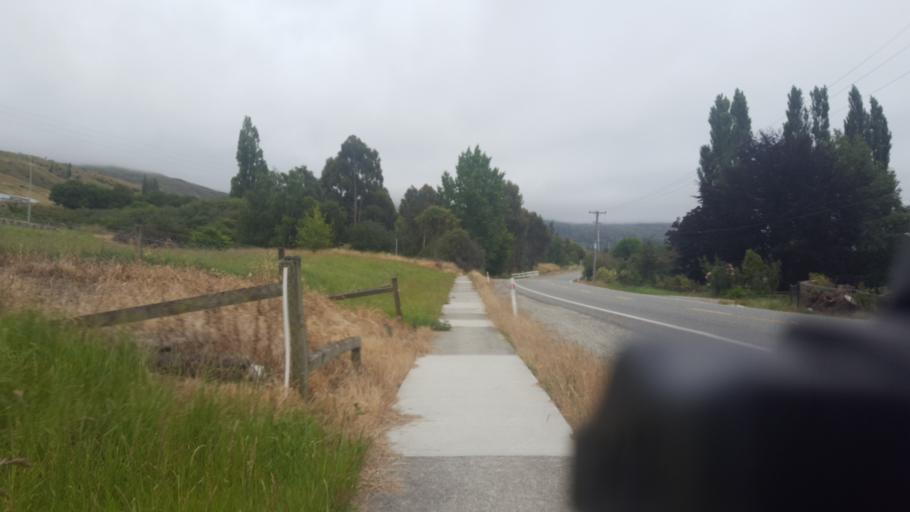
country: NZ
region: Otago
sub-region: Queenstown-Lakes District
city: Kingston
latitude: -45.5331
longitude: 169.3002
